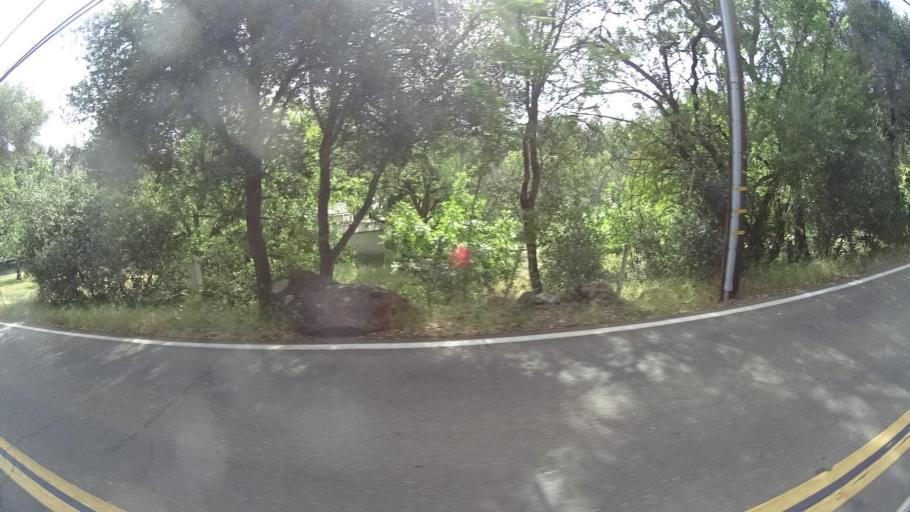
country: US
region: California
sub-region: Lake County
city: Soda Bay
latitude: 38.9726
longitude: -122.7435
